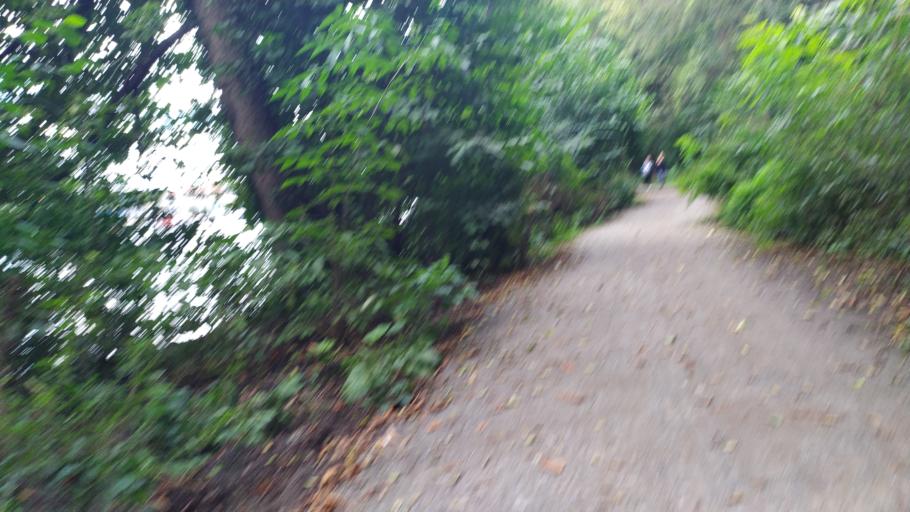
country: DE
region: Berlin
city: Friedrichshagen
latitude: 52.4481
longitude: 13.6038
